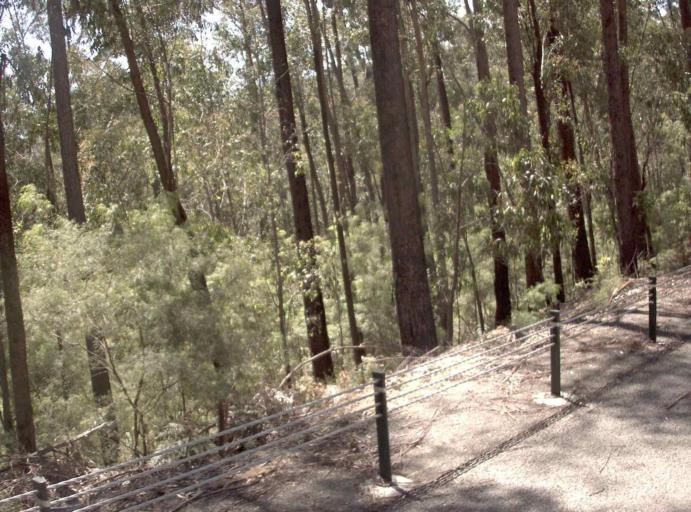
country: AU
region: New South Wales
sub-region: Bombala
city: Bombala
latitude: -37.5873
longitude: 148.9910
